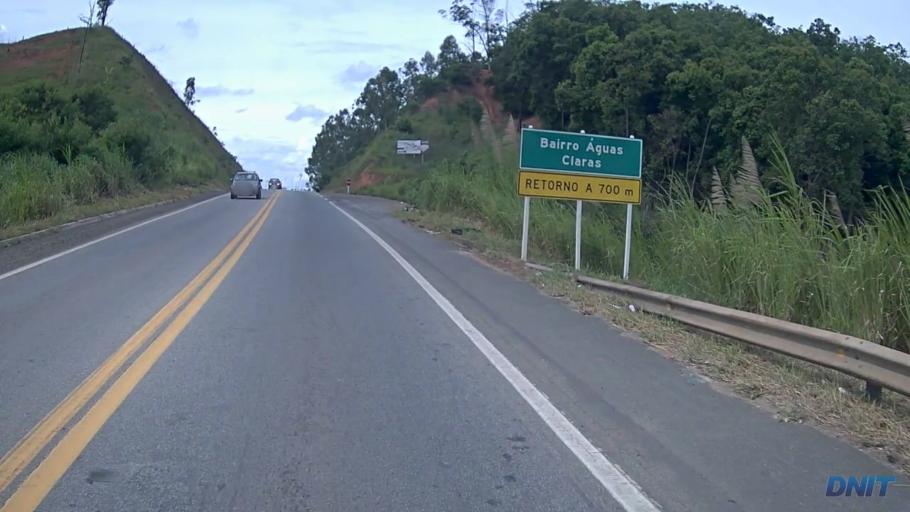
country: BR
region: Minas Gerais
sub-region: Ipatinga
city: Ipatinga
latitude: -19.4473
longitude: -42.5146
